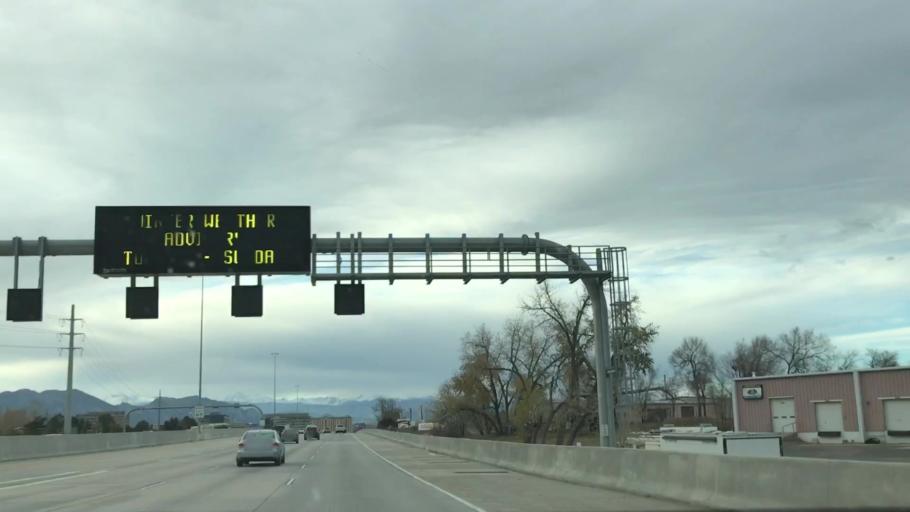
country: US
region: Colorado
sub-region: Broomfield County
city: Broomfield
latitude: 39.9196
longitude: -105.1008
